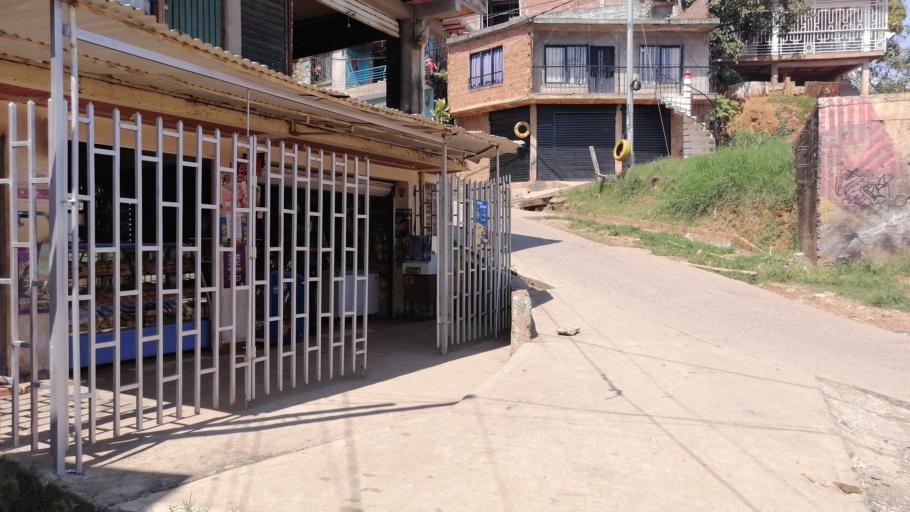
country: CO
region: Valle del Cauca
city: Cali
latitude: 3.3793
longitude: -76.5585
